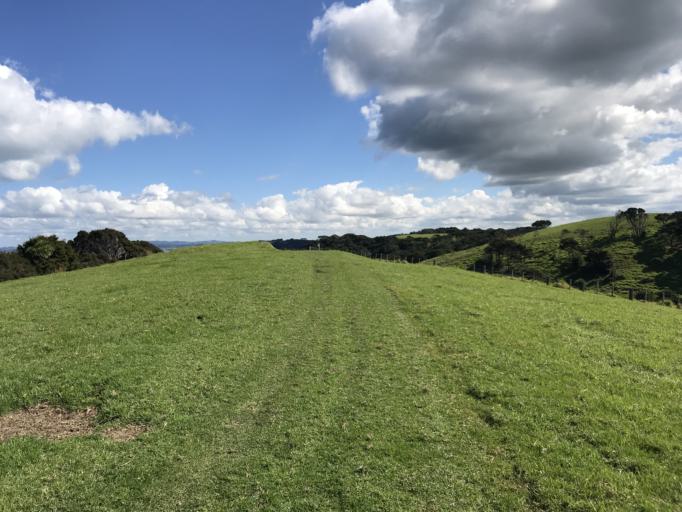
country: NZ
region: Auckland
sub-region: Auckland
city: Warkworth
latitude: -36.3759
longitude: 174.8351
